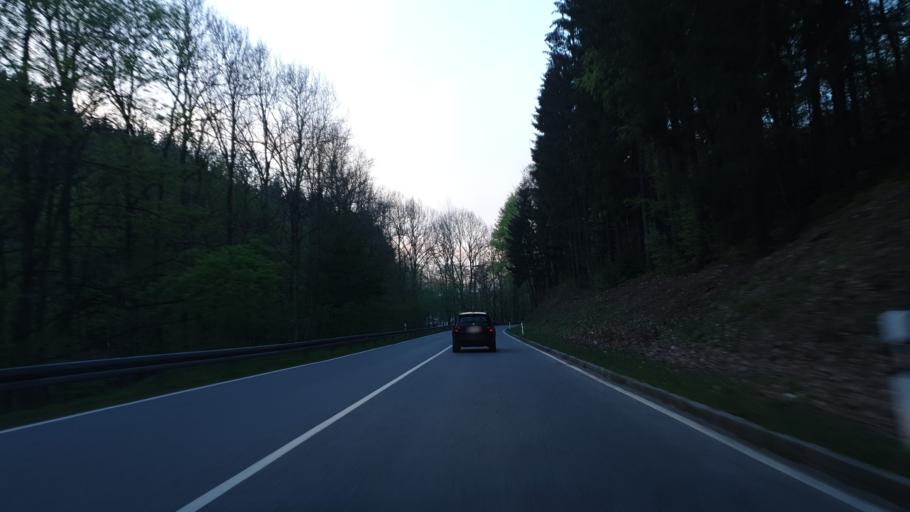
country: DE
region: Saxony
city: Aue
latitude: 50.6050
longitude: 12.7187
